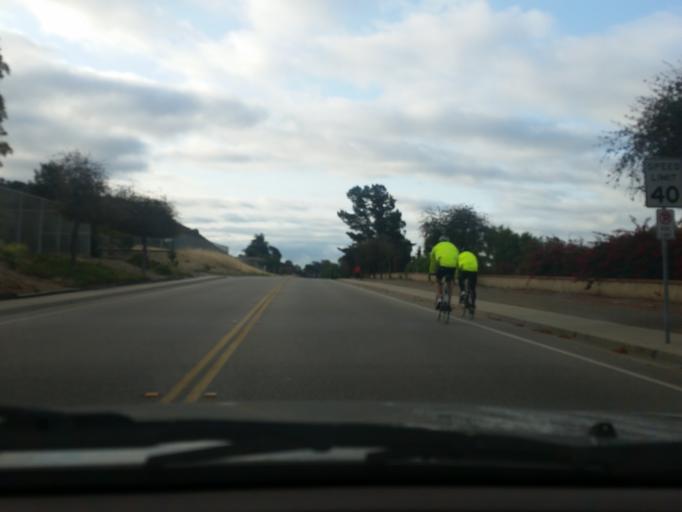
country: US
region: California
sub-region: San Luis Obispo County
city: Avila Beach
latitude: 35.1726
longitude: -120.6965
